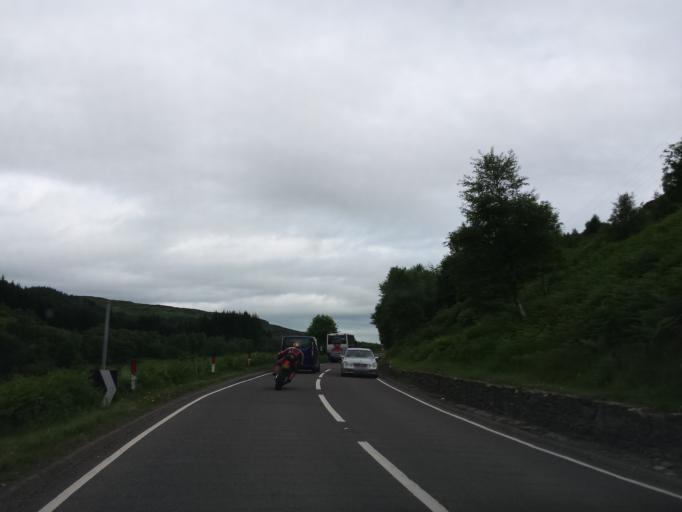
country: GB
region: Scotland
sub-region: Stirling
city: Callander
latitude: 56.4148
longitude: -4.3253
